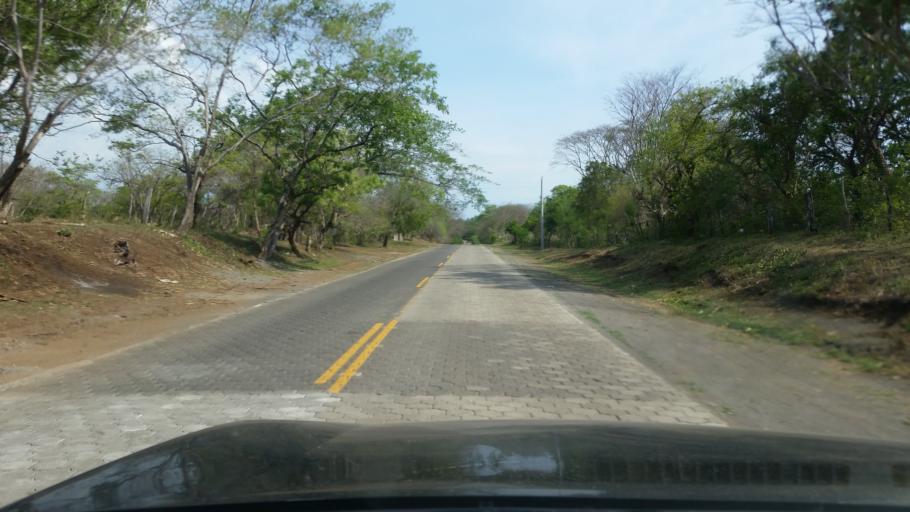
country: NI
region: Managua
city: Carlos Fonseca Amador
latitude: 12.0092
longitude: -86.5174
